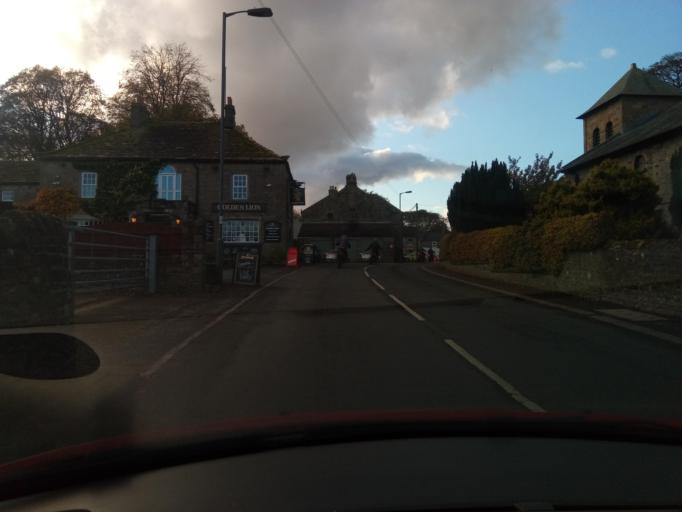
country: GB
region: England
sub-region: County Durham
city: Newbiggin
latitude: 54.7360
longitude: -2.1789
